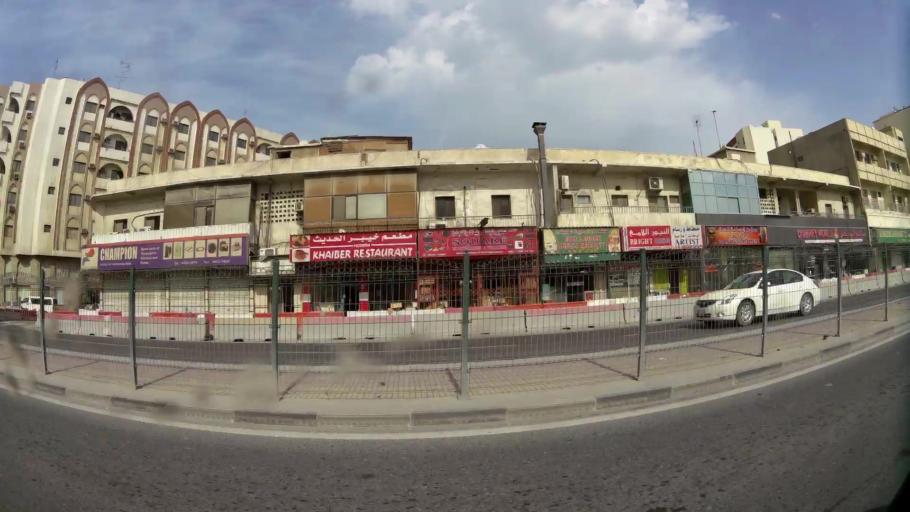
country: QA
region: Baladiyat ad Dawhah
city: Doha
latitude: 25.2828
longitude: 51.5176
